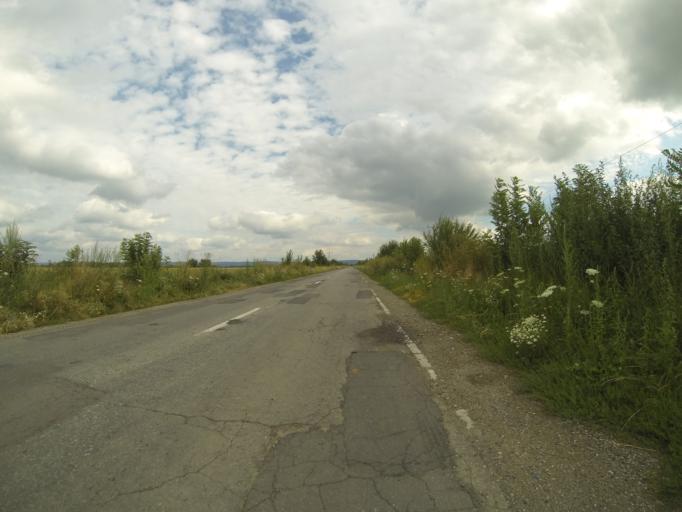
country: RO
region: Brasov
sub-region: Comuna Sercaia
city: Sercaia
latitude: 45.8081
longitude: 25.1464
